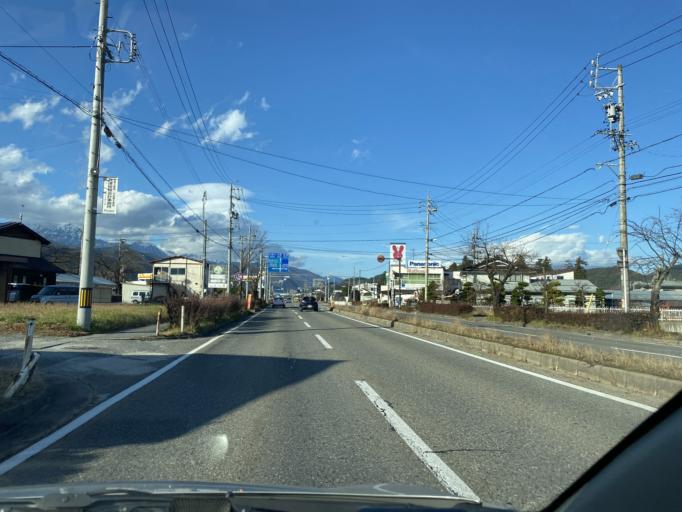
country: JP
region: Nagano
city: Omachi
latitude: 36.5120
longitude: 137.8527
